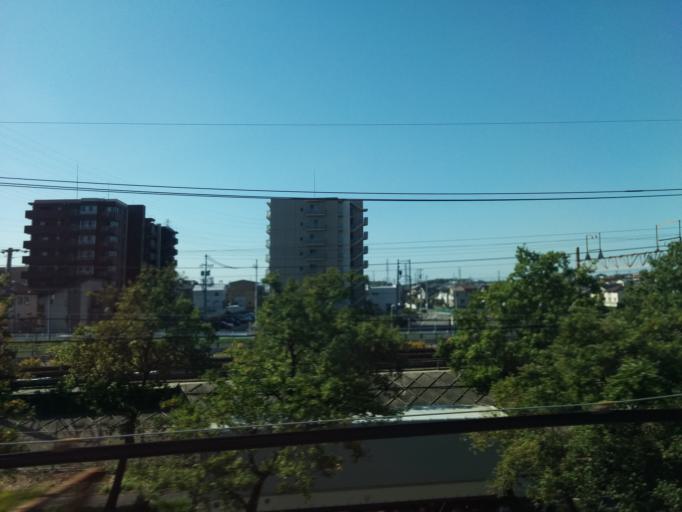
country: JP
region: Aichi
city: Obu
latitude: 35.0580
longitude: 136.9473
